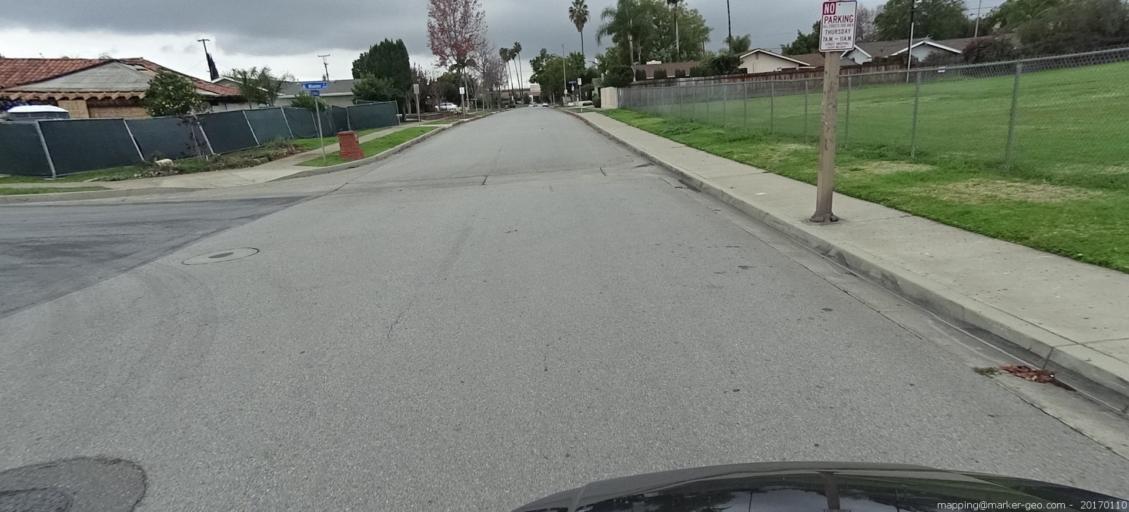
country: US
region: California
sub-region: Orange County
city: Orange
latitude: 33.7773
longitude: -117.8241
